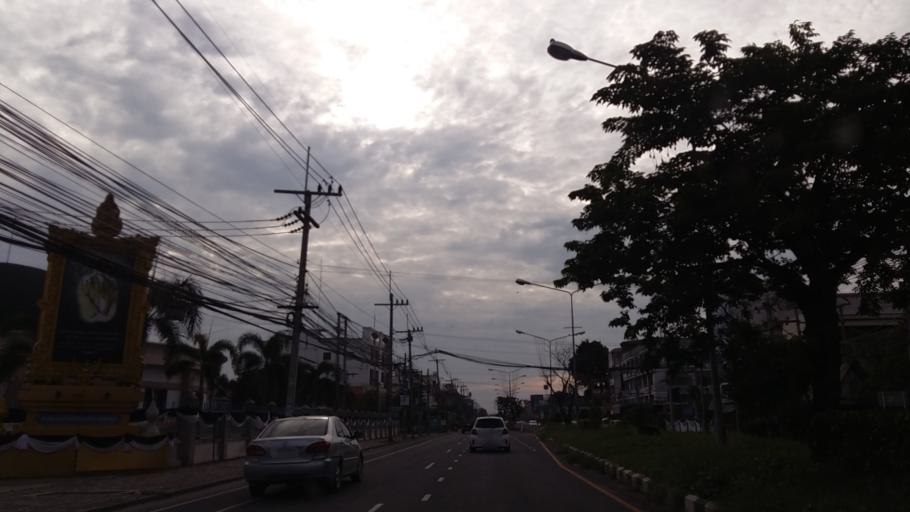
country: TH
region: Chon Buri
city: Chon Buri
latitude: 13.3391
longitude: 100.9559
